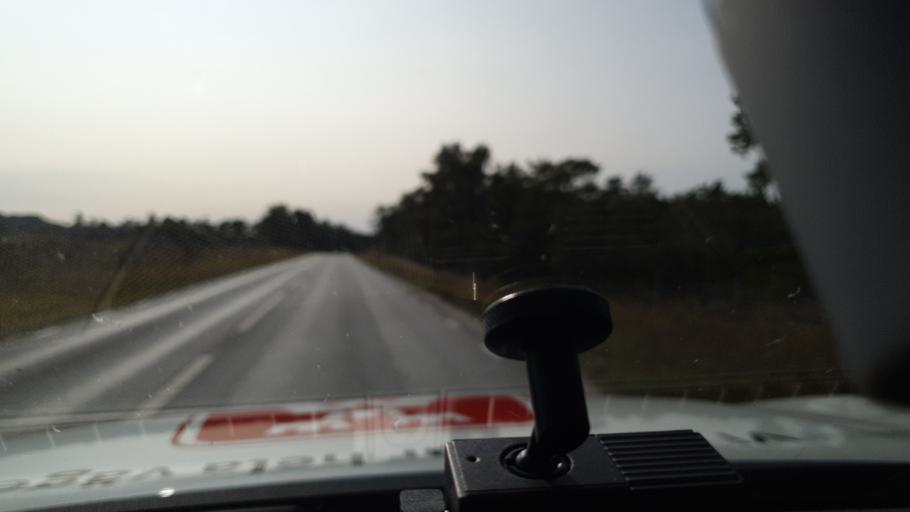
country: SE
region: Gotland
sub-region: Gotland
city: Slite
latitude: 57.8259
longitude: 18.8971
